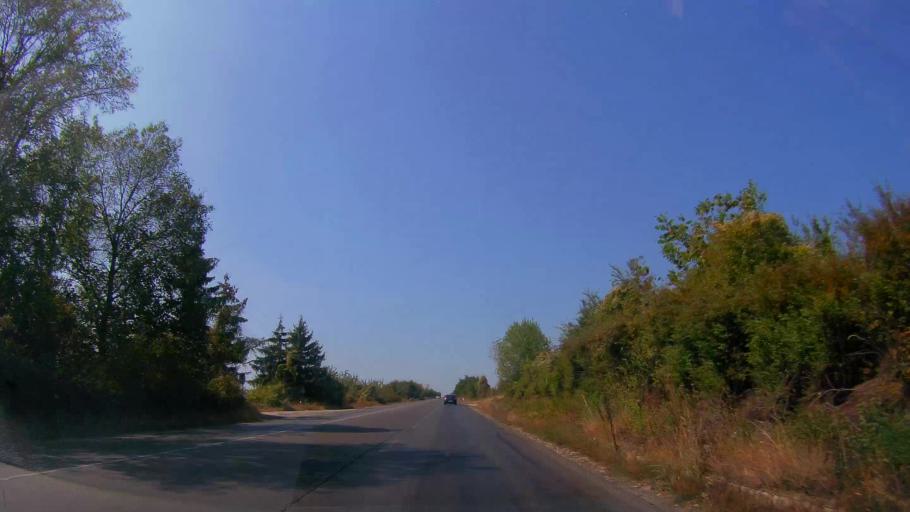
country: BG
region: Ruse
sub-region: Obshtina Vetovo
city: Senovo
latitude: 43.5607
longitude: 26.3717
